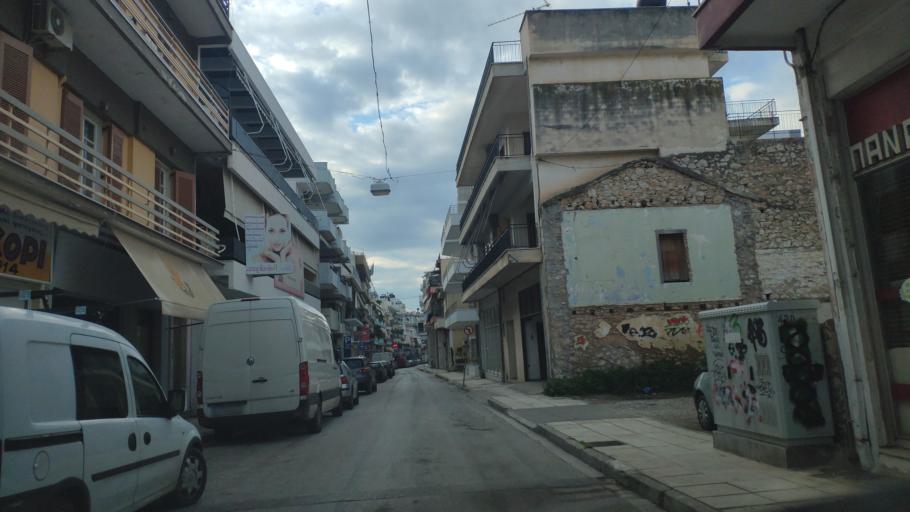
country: GR
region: Peloponnese
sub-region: Nomos Argolidos
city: Argos
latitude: 37.6391
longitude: 22.7290
